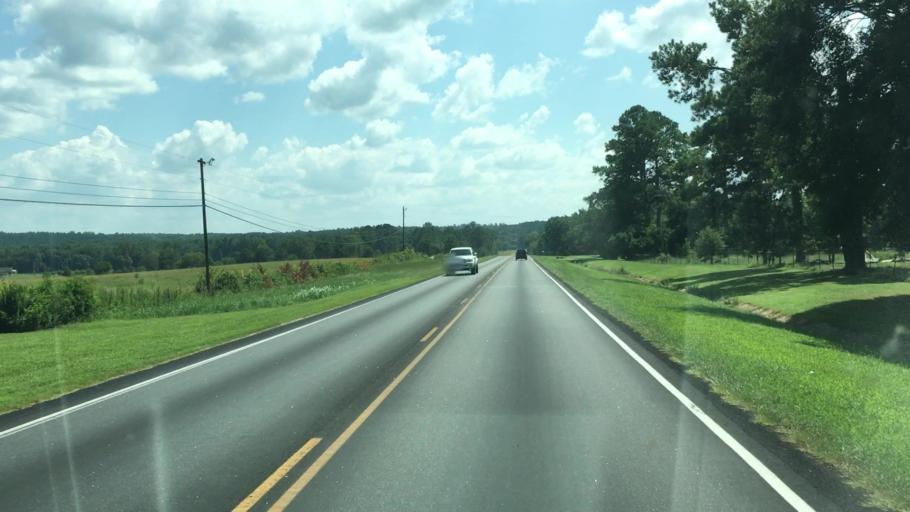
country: US
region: Georgia
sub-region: Morgan County
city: Madison
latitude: 33.6529
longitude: -83.4468
